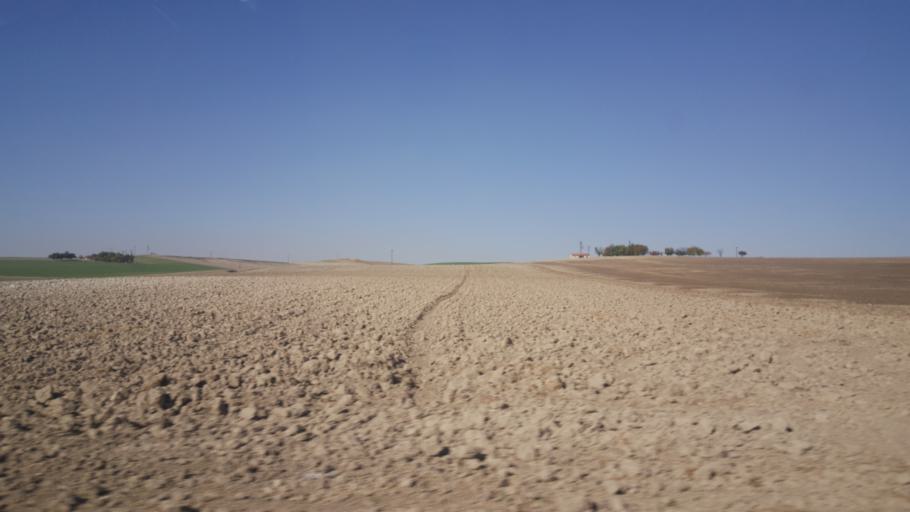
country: TR
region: Konya
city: Celtik
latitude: 39.0665
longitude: 31.8978
